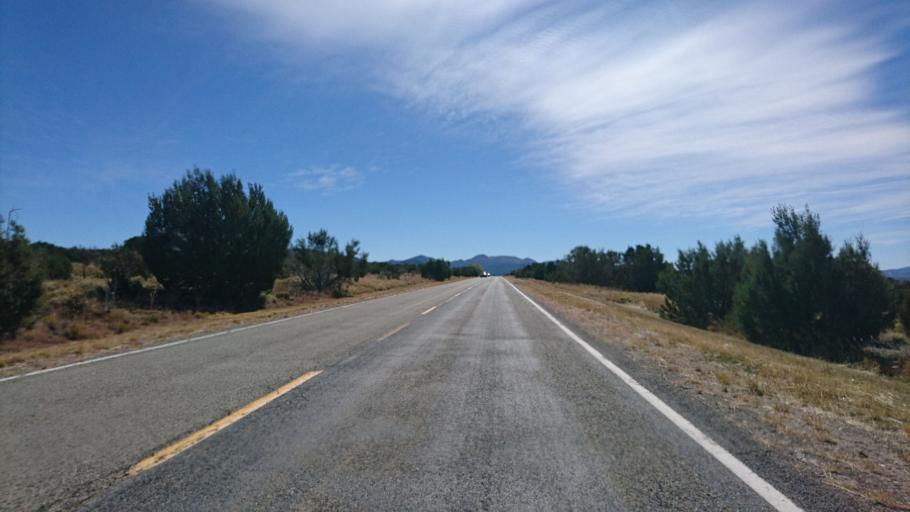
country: US
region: New Mexico
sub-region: Bernalillo County
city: Sandia Knolls
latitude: 35.3189
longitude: -106.2151
